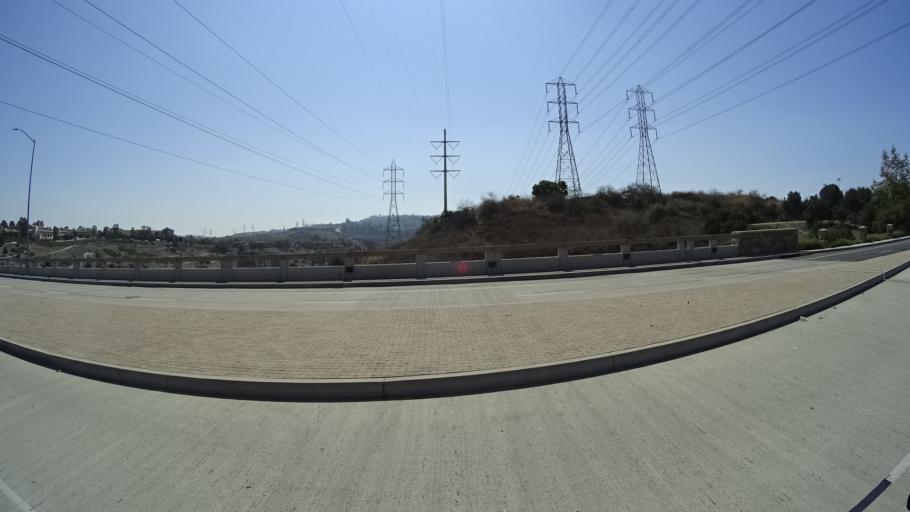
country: US
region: California
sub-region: Orange County
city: San Clemente
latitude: 33.4647
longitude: -117.6035
